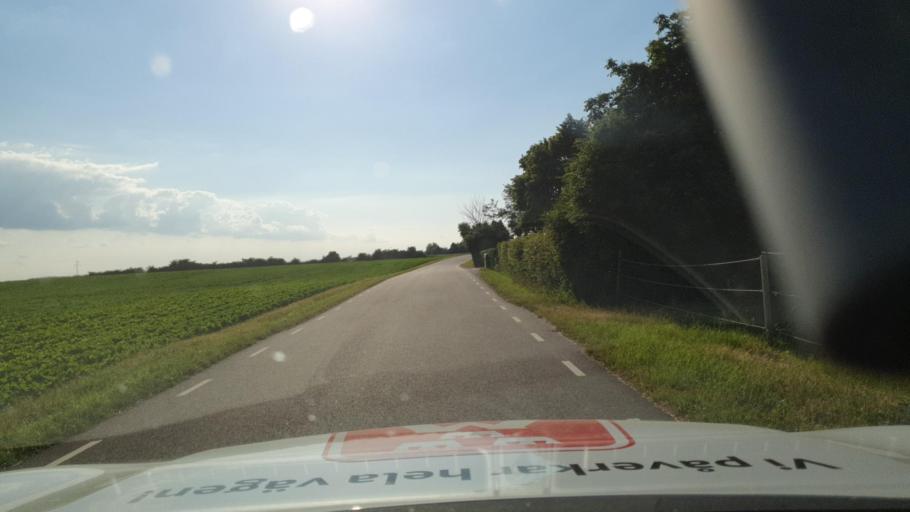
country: SE
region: Skane
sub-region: Skurups Kommun
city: Rydsgard
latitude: 55.5035
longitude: 13.5742
